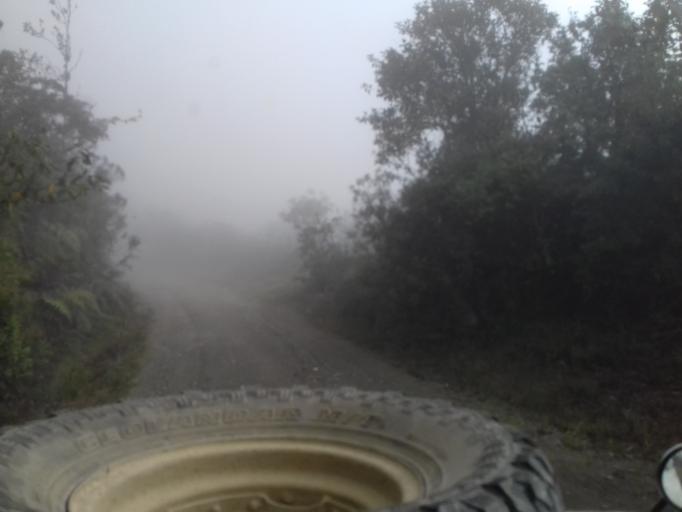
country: CO
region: Quindio
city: Salento
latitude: 4.5524
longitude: -75.5156
